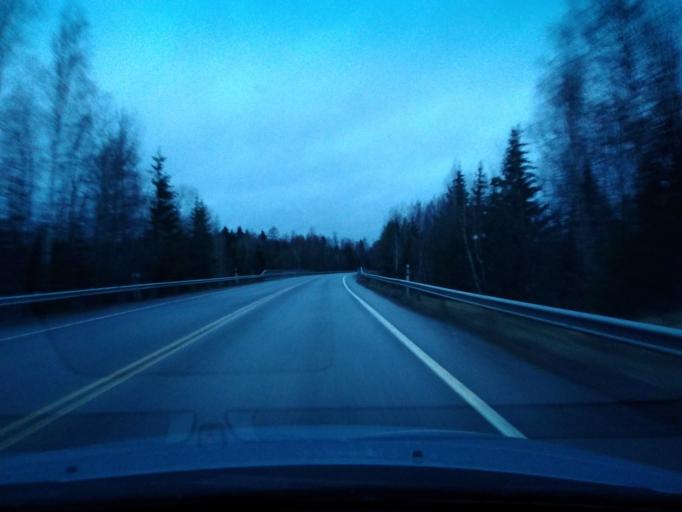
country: FI
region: Uusimaa
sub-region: Porvoo
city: Porvoo
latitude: 60.4073
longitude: 25.5860
